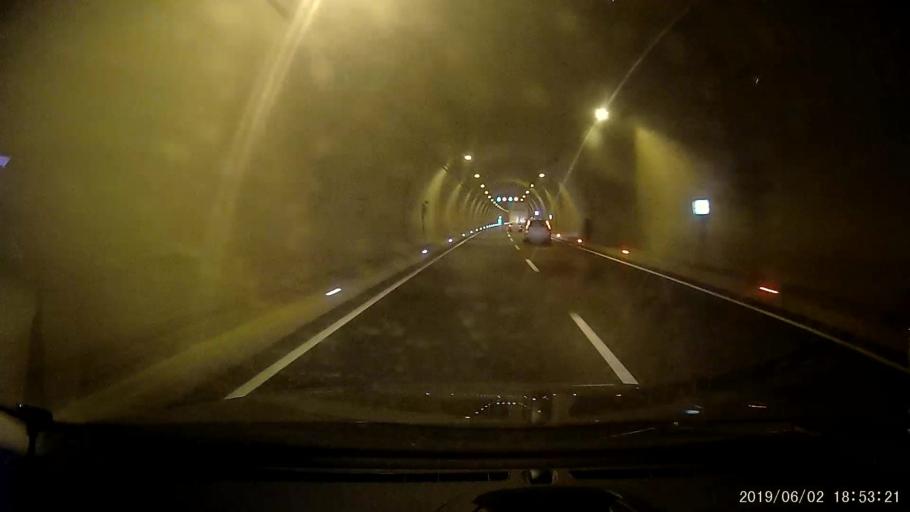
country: TR
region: Ordu
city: Ordu
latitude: 40.9800
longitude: 37.8299
